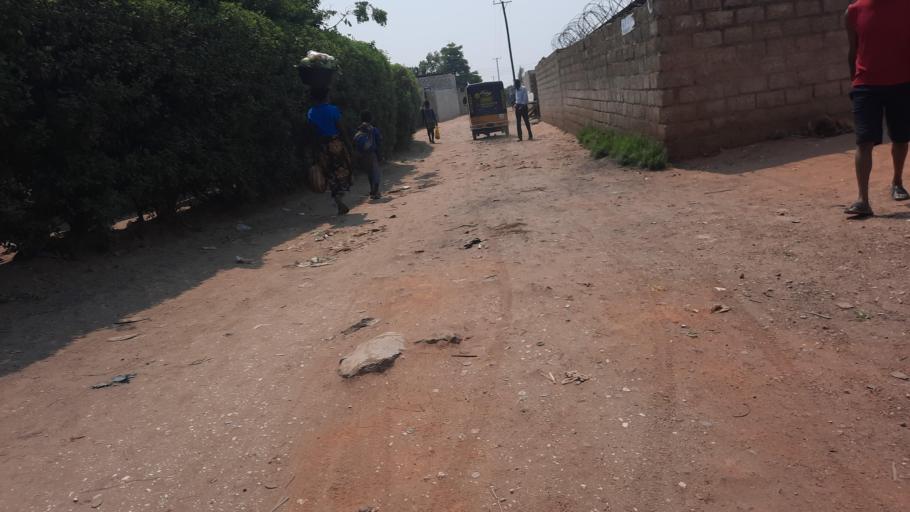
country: ZM
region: Lusaka
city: Lusaka
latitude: -15.4067
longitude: 28.3710
